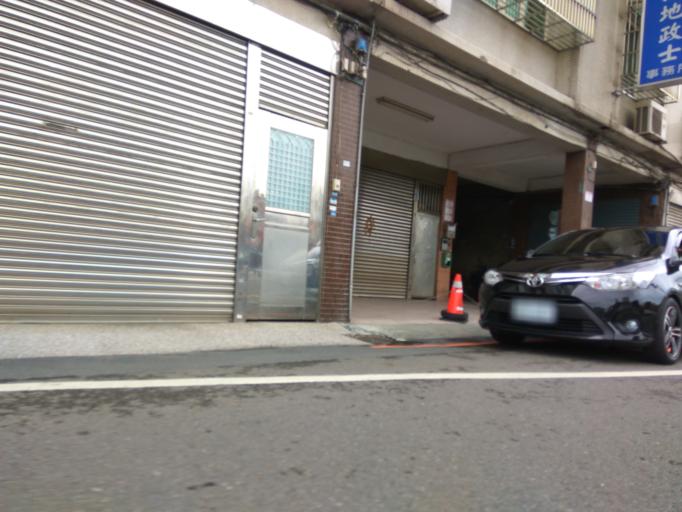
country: TW
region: Taiwan
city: Taoyuan City
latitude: 24.9587
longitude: 121.2182
